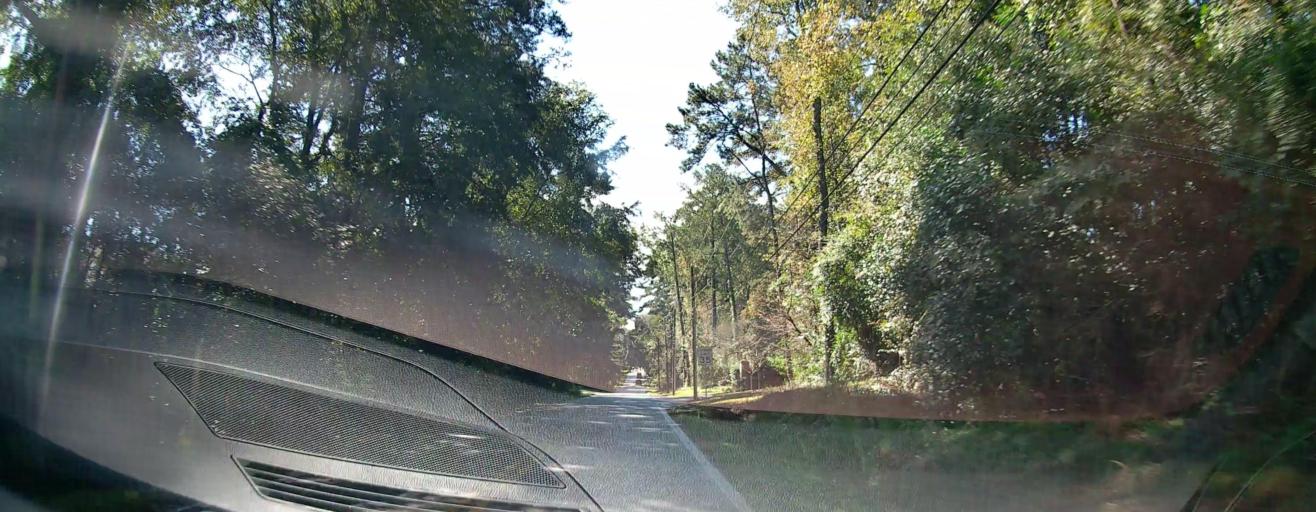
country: US
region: Georgia
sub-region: Bibb County
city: Macon
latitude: 32.8895
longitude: -83.7174
